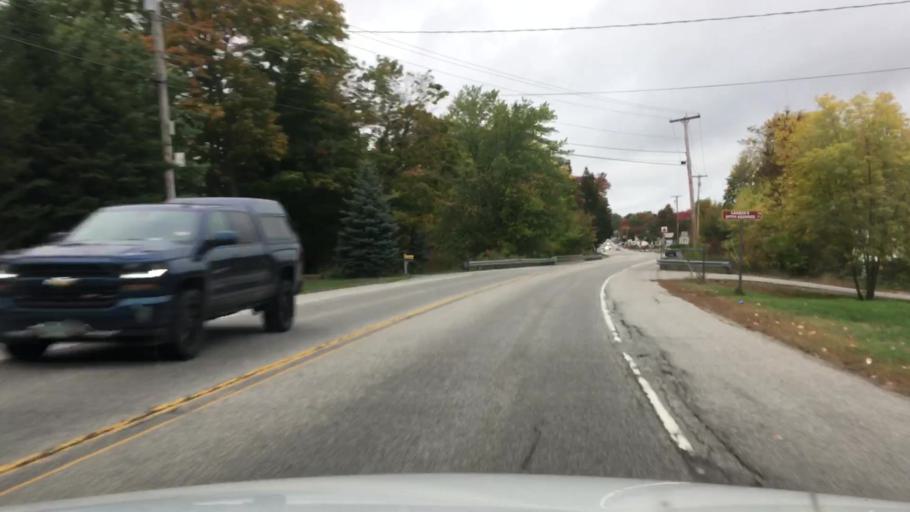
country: US
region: Maine
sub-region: Oxford County
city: Oxford
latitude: 44.1317
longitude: -70.4616
